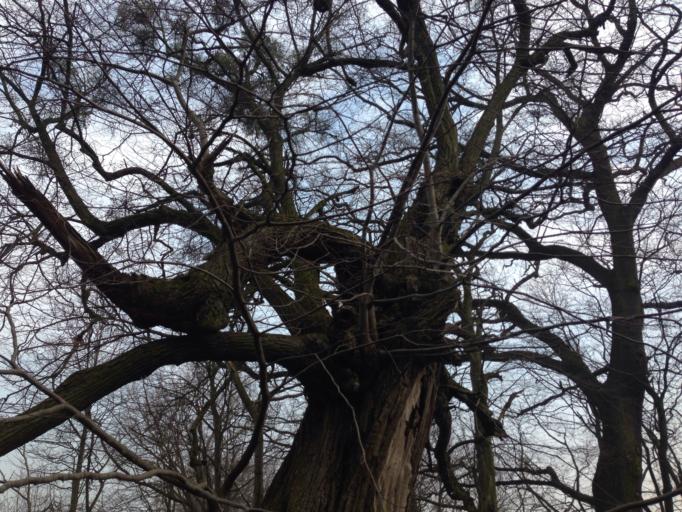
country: PL
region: Pomeranian Voivodeship
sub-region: Powiat kwidzynski
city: Sadlinki
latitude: 53.7193
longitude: 18.8134
